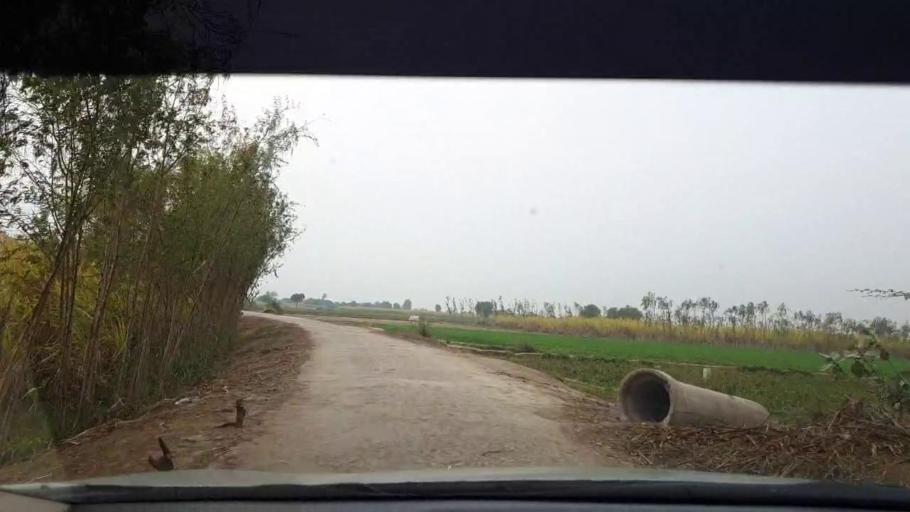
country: PK
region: Sindh
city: Berani
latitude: 25.8648
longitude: 68.7942
